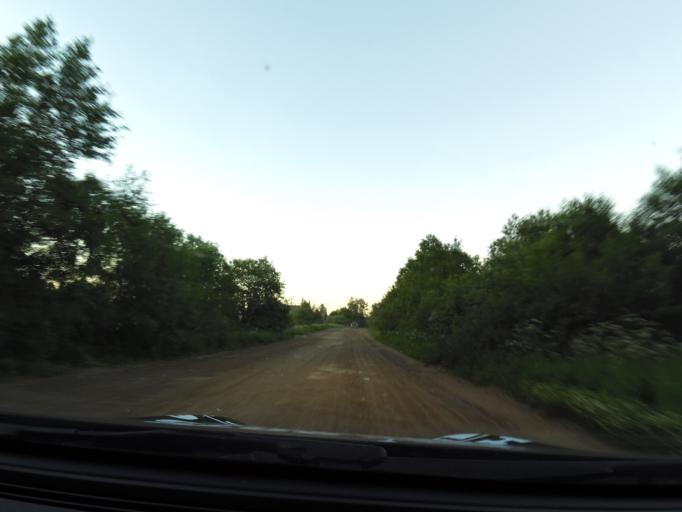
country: RU
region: Leningrad
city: Voznesen'ye
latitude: 60.8377
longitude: 35.7704
